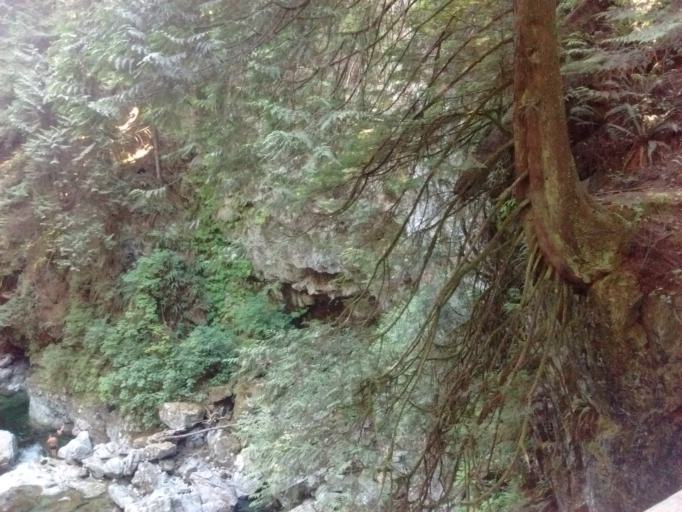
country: CA
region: British Columbia
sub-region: Fraser Valley Regional District
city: North Vancouver
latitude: 49.3412
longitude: -123.0159
